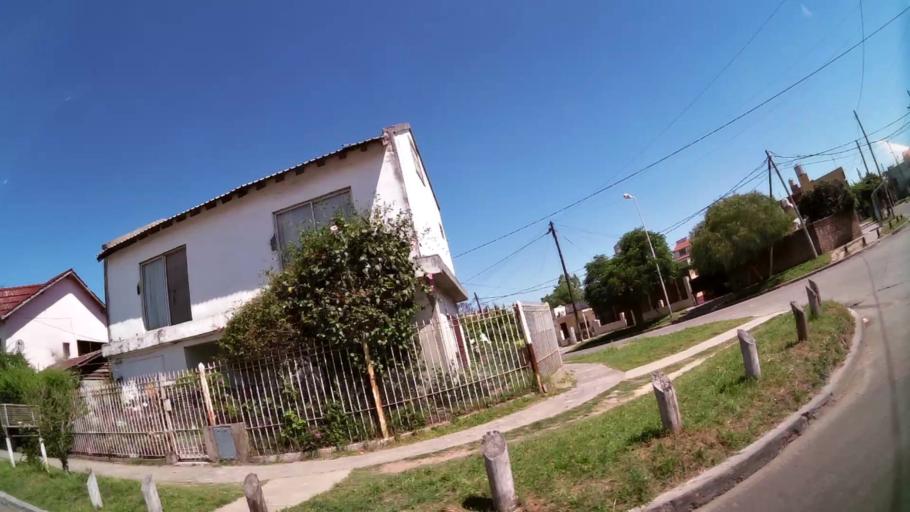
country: AR
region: Buenos Aires
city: Hurlingham
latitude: -34.5057
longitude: -58.6692
